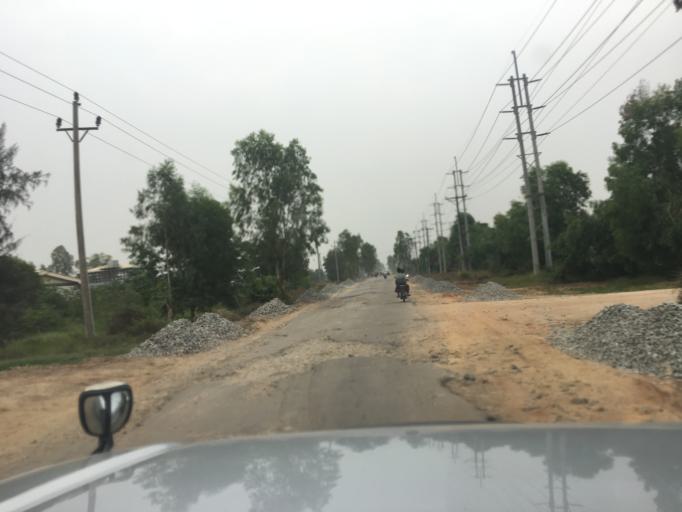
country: MM
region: Yangon
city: Syriam
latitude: 16.9542
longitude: 96.2701
